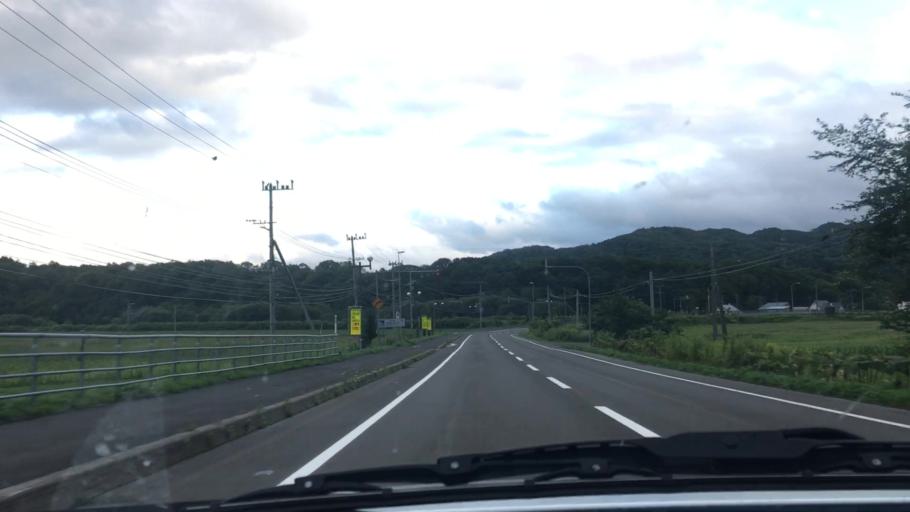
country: JP
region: Hokkaido
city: Shimo-furano
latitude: 42.9860
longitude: 142.3990
